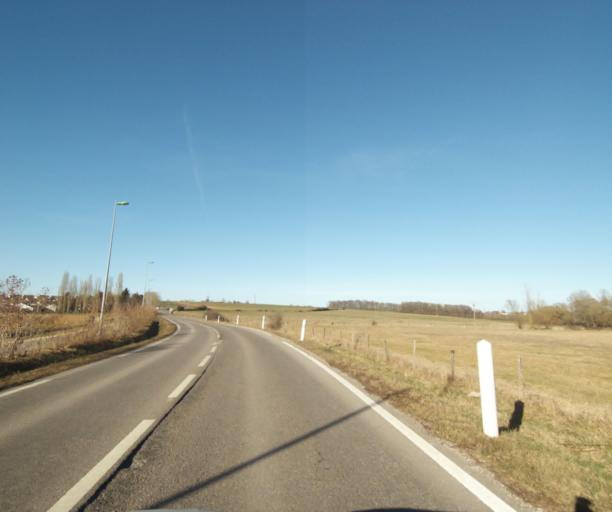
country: FR
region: Lorraine
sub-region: Departement de Meurthe-et-Moselle
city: Fleville-devant-Nancy
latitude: 48.6395
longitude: 6.2115
